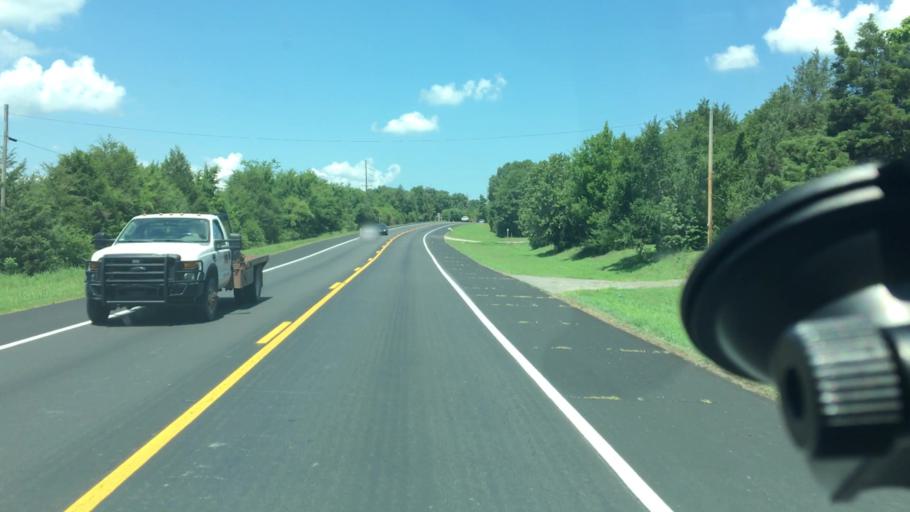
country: US
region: Arkansas
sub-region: Sebastian County
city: Lavaca
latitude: 35.2985
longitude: -94.1548
